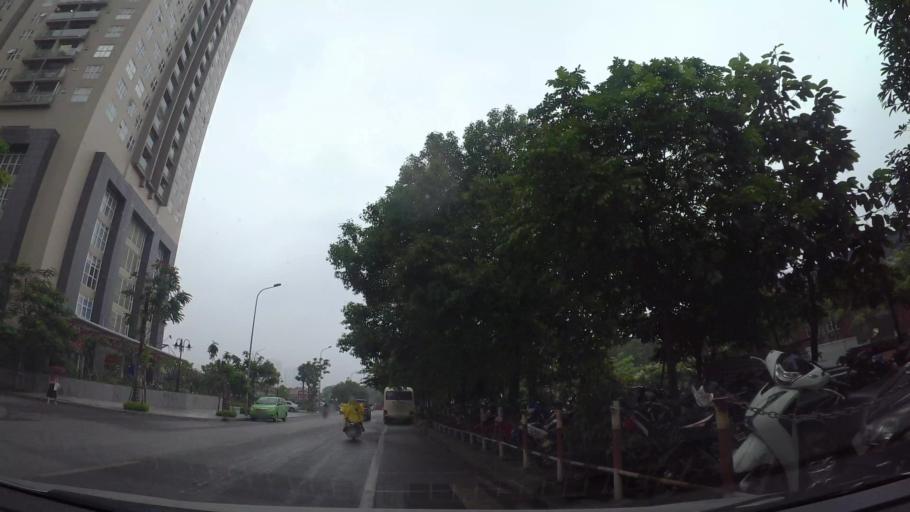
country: VN
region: Ha Noi
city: Thanh Xuan
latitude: 21.0098
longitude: 105.7935
